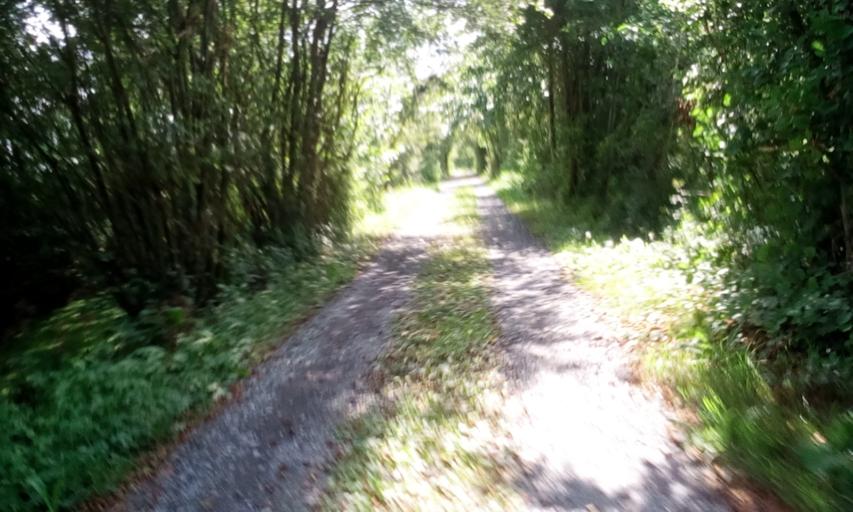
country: FR
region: Lower Normandy
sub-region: Departement du Calvados
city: Bavent
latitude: 49.2346
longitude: -0.1658
